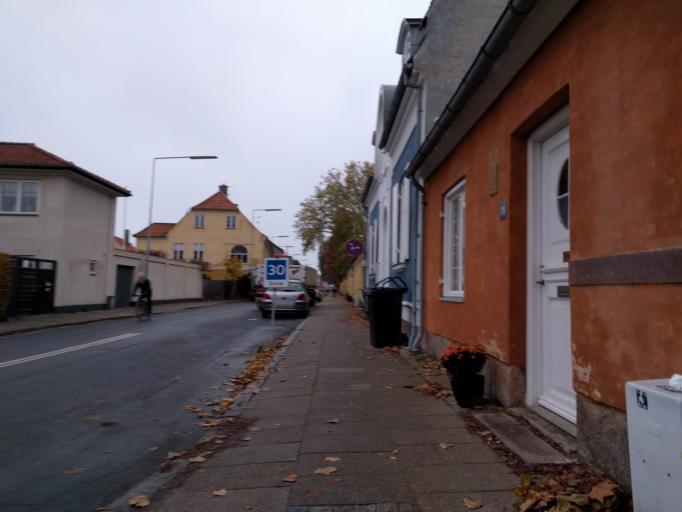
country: DK
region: Capital Region
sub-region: Helsingor Kommune
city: Helsingor
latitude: 56.0403
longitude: 12.6061
